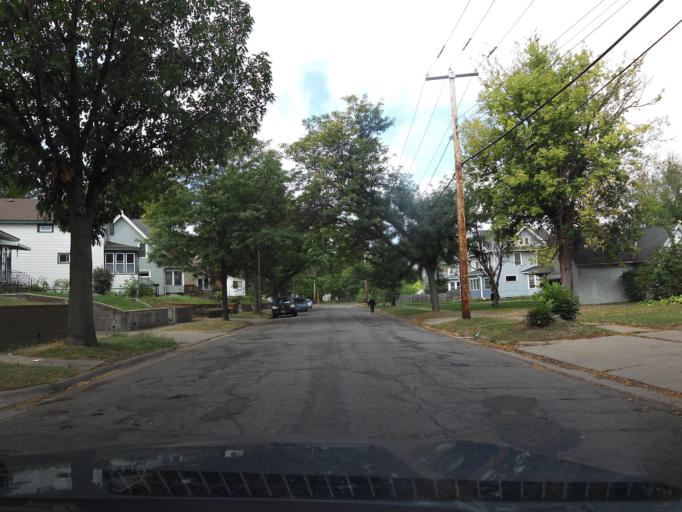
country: US
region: Minnesota
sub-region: Ramsey County
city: Saint Paul
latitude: 44.9597
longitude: -93.1003
